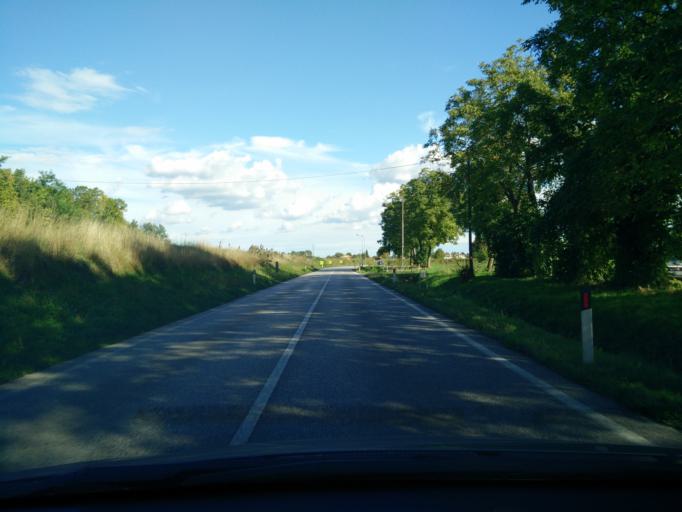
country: IT
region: Veneto
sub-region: Provincia di Treviso
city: Candelu
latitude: 45.7405
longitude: 12.3566
